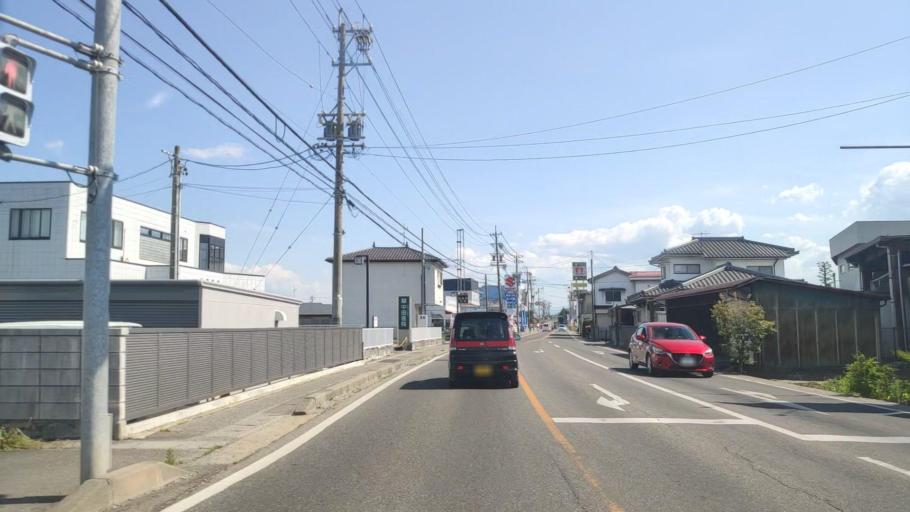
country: JP
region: Nagano
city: Hotaka
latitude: 36.3240
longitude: 137.8934
